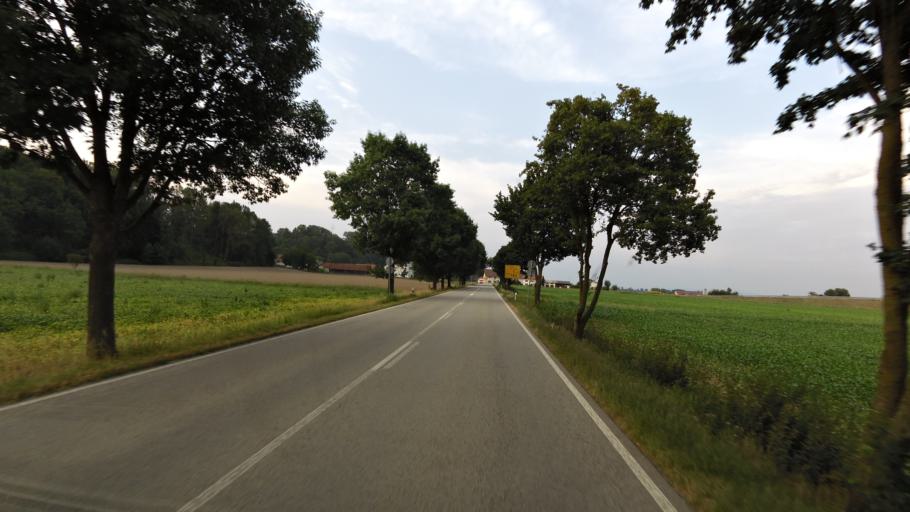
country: DE
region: Bavaria
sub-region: Lower Bavaria
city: Rotthalmunster
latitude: 48.3321
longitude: 13.2248
